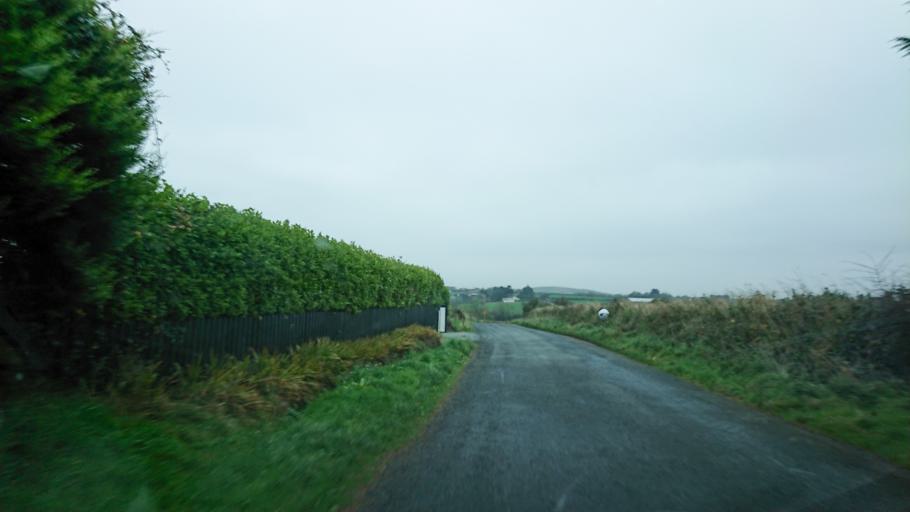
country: IE
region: Munster
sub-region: Waterford
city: Dunmore East
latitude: 52.1653
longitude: -7.0273
